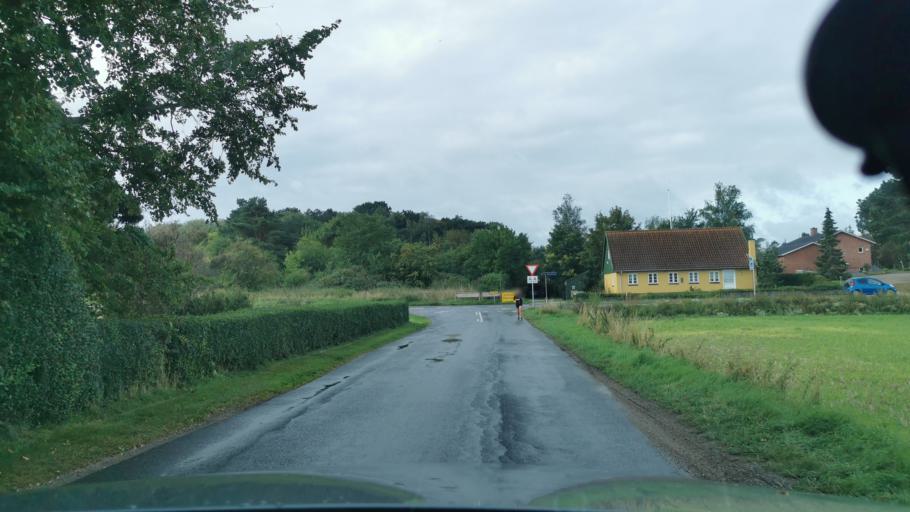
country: DK
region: Zealand
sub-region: Kalundborg Kommune
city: Kalundborg
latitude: 55.7290
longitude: 10.9964
